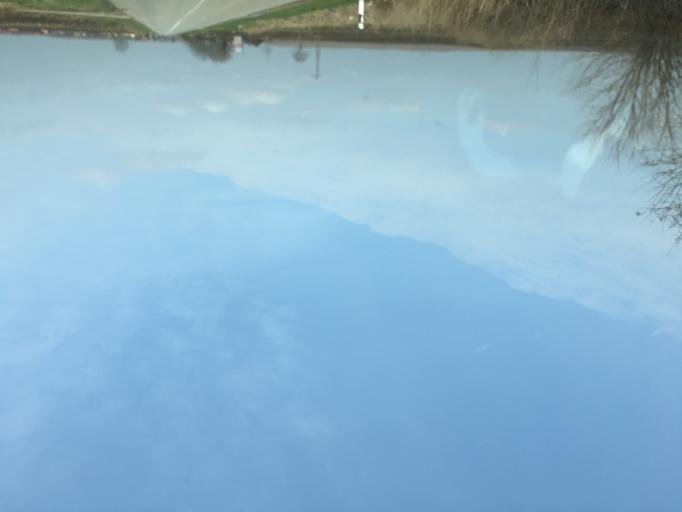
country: RS
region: Autonomna Pokrajina Vojvodina
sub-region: Juznobanatski Okrug
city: Opovo
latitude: 45.0668
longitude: 20.4372
